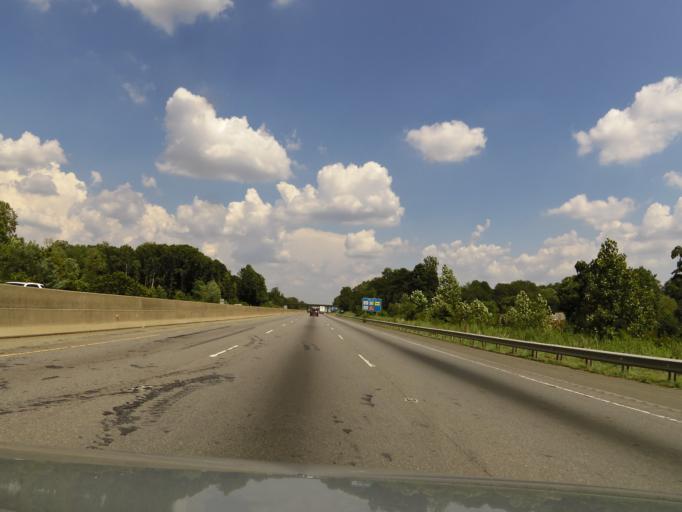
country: US
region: North Carolina
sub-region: Gaston County
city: Bessemer City
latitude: 35.2726
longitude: -81.2408
